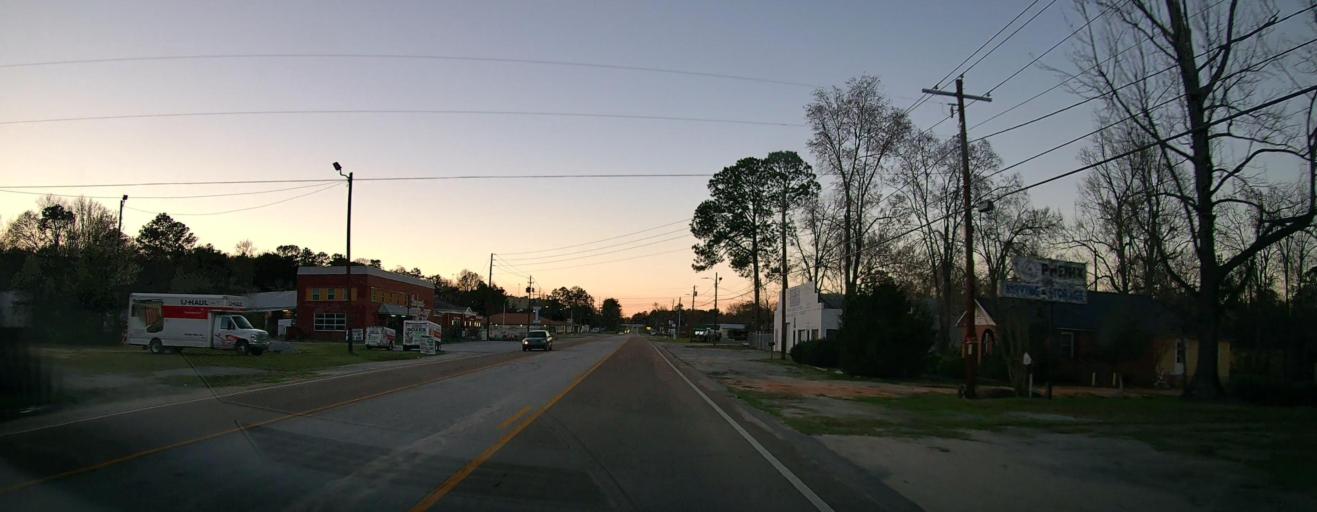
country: US
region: Alabama
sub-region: Russell County
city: Phenix City
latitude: 32.4770
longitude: -85.0256
